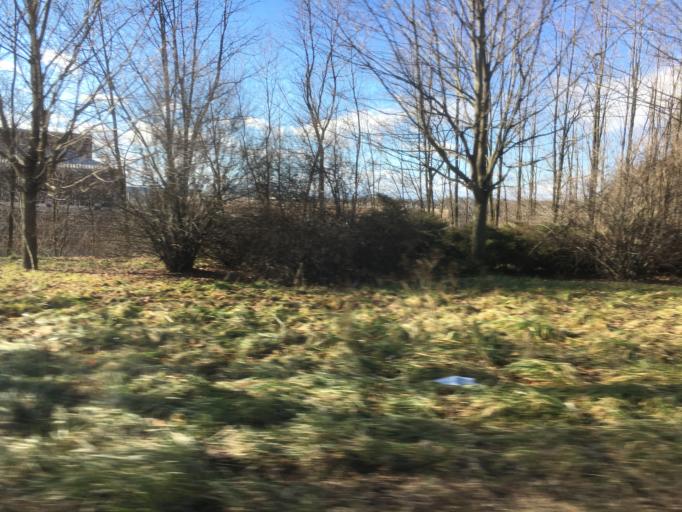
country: US
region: Pennsylvania
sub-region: Lehigh County
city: Egypt
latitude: 40.6404
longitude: -75.5447
